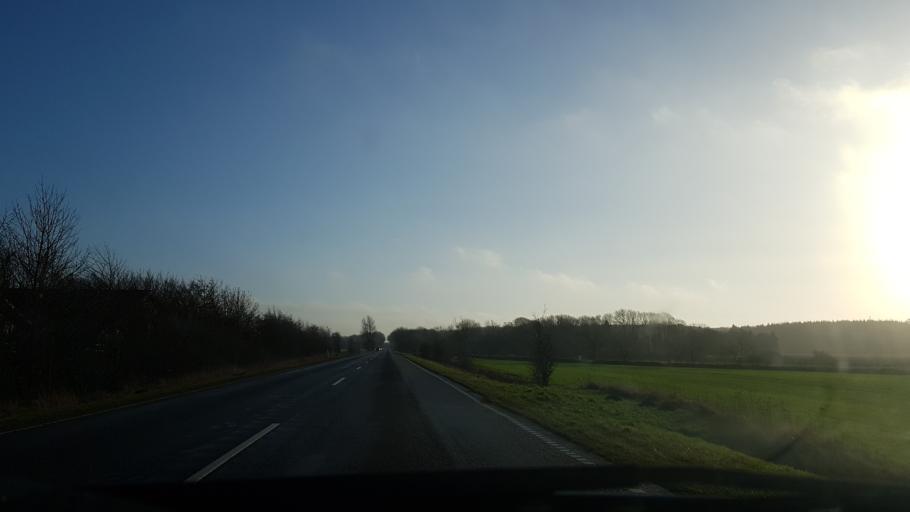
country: DK
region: South Denmark
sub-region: Tonder Kommune
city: Toftlund
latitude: 55.2296
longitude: 9.1703
